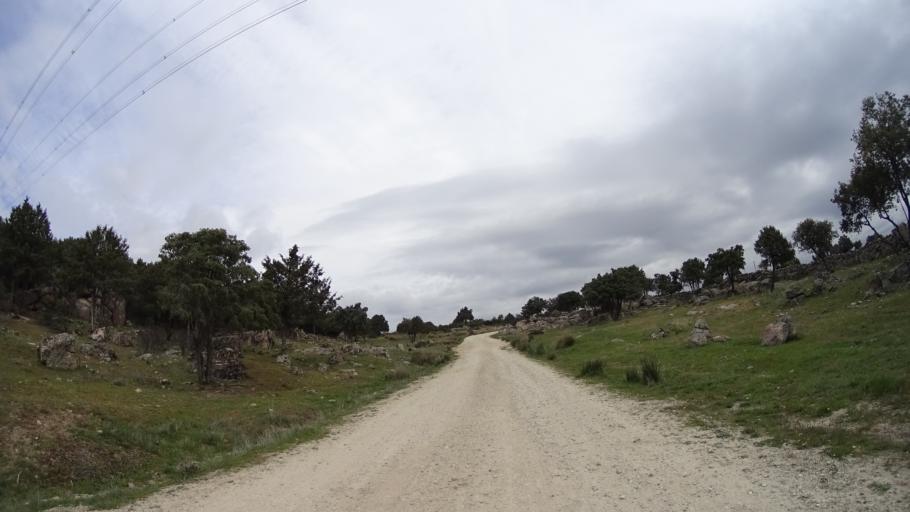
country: ES
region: Madrid
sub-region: Provincia de Madrid
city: Hoyo de Manzanares
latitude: 40.6141
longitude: -3.8793
